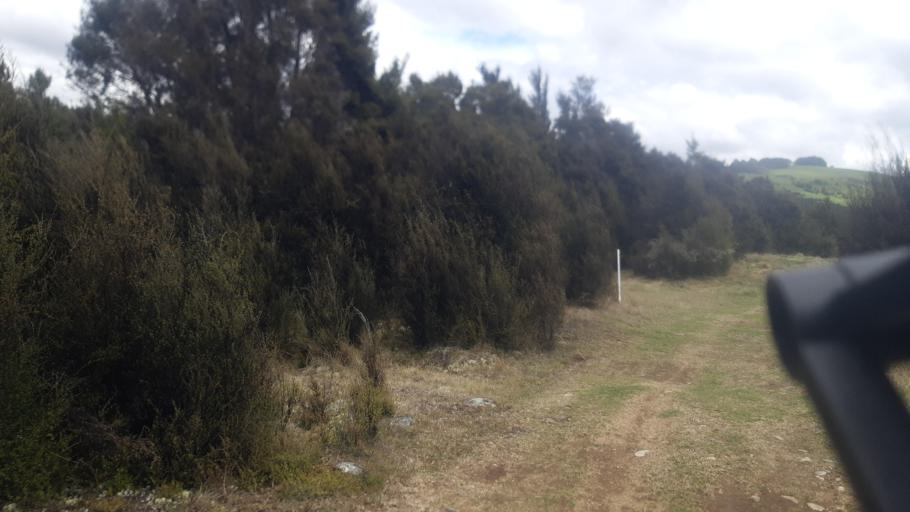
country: NZ
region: Tasman
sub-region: Tasman District
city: Wakefield
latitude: -41.7905
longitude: 172.8276
